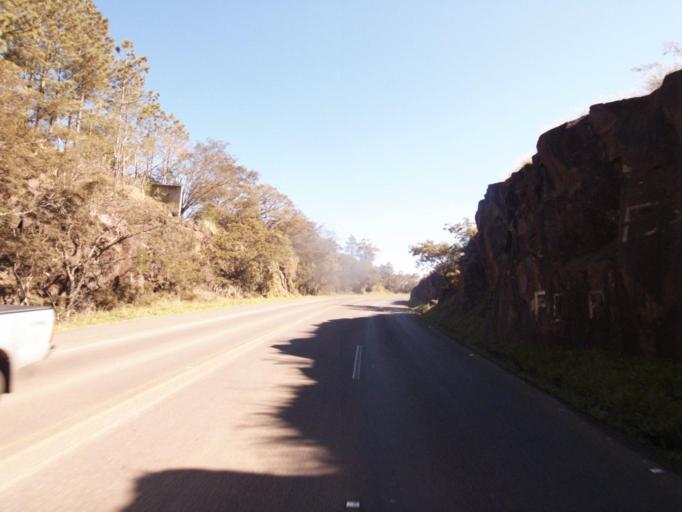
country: AR
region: Misiones
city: Bernardo de Irigoyen
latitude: -26.7660
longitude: -53.4912
